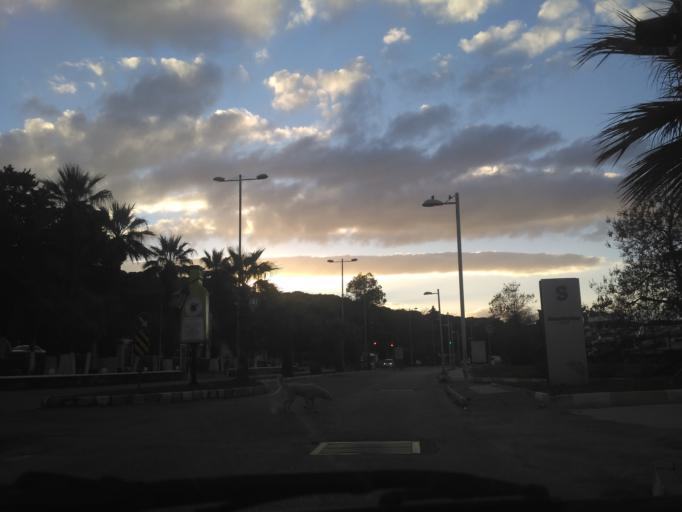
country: TR
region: Balikesir
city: Ayvalik
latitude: 39.3120
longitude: 26.6870
